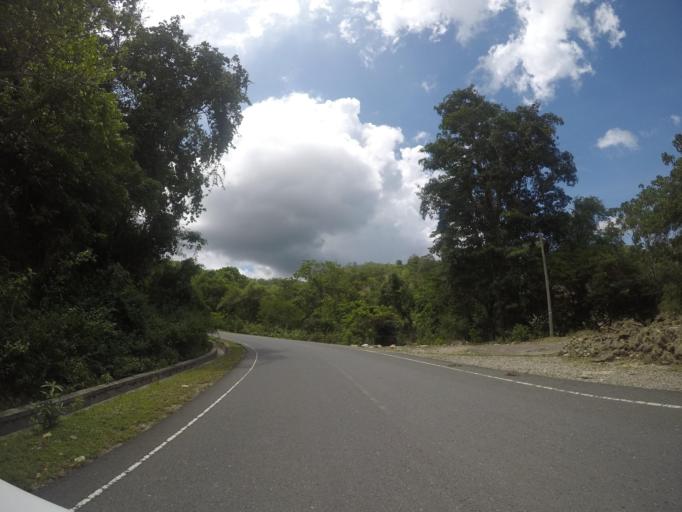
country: TL
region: Bobonaro
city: Maliana
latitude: -8.9501
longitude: 125.1015
